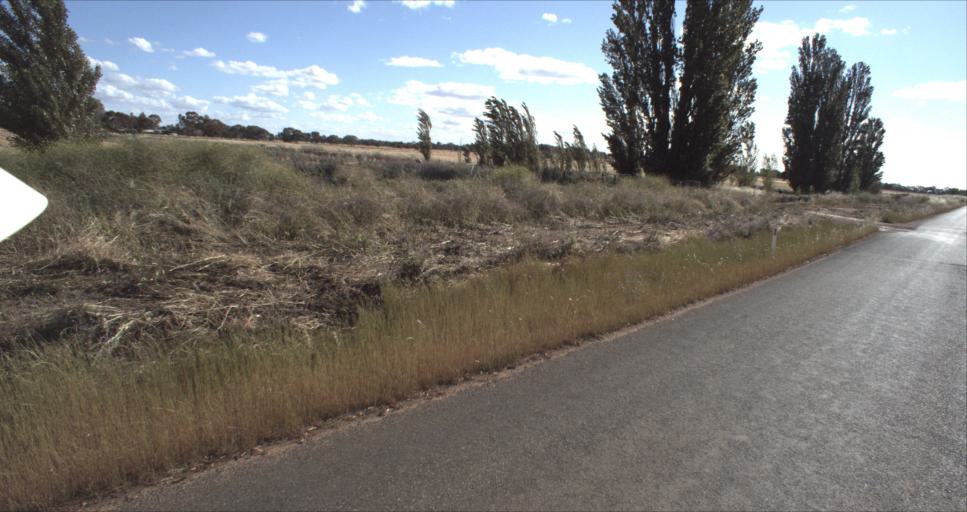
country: AU
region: New South Wales
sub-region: Griffith
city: Griffith
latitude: -34.4383
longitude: 146.2085
